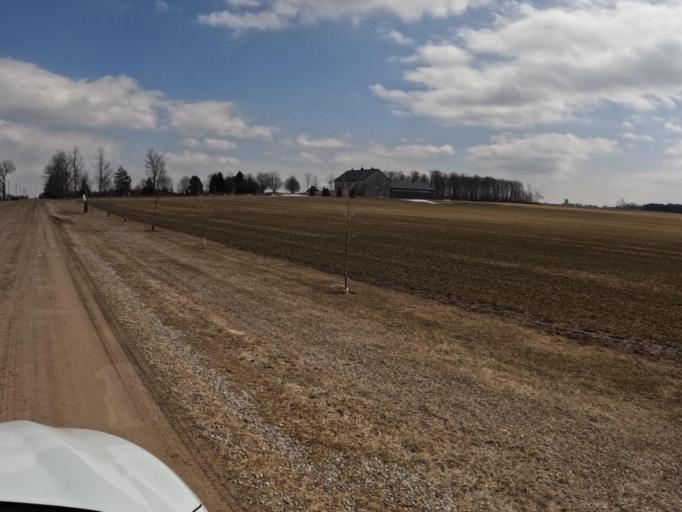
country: CA
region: Ontario
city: Shelburne
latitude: 44.0656
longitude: -80.2151
